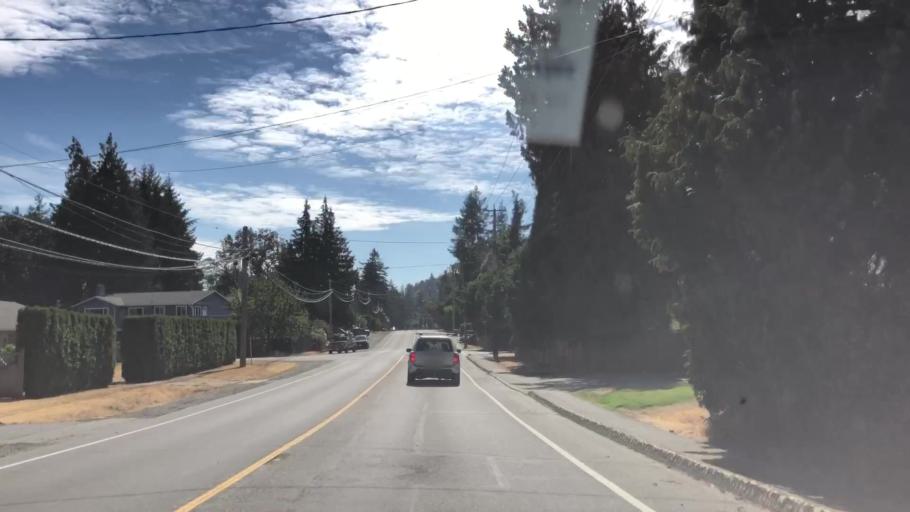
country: CA
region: British Columbia
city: Colwood
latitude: 48.4257
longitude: -123.4909
